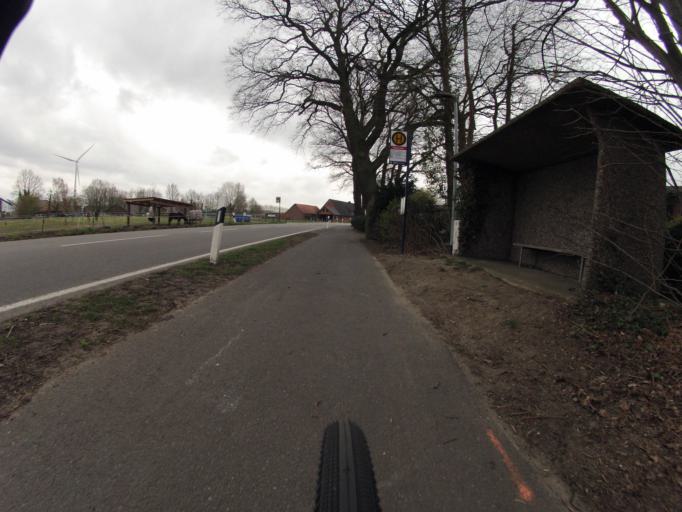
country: DE
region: North Rhine-Westphalia
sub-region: Regierungsbezirk Munster
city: Mettingen
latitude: 52.3452
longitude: 7.7838
